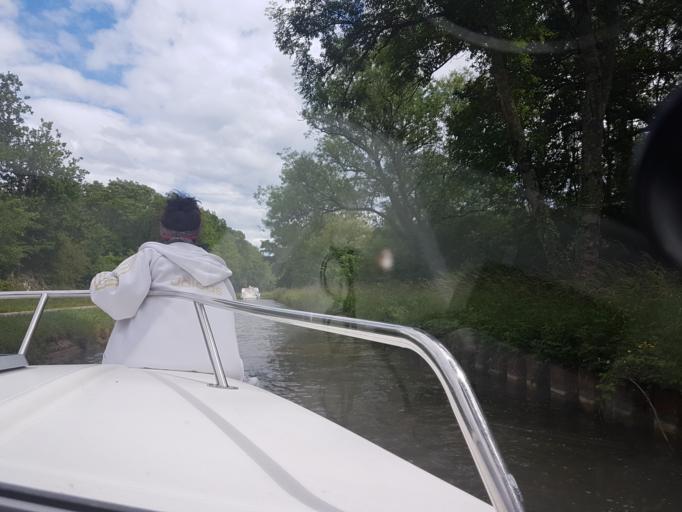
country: FR
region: Bourgogne
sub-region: Departement de l'Yonne
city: Vermenton
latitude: 47.5893
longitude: 3.6377
